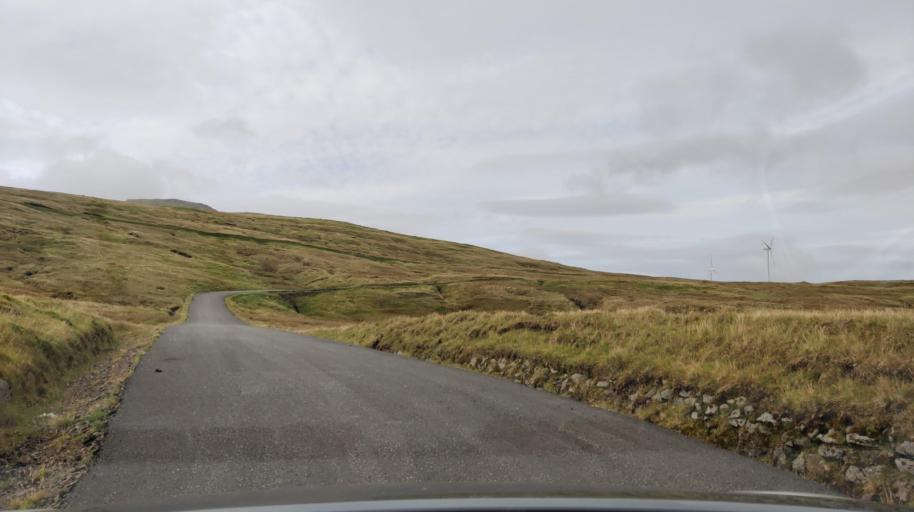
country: FO
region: Streymoy
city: Vestmanna
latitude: 62.1586
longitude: -7.1015
